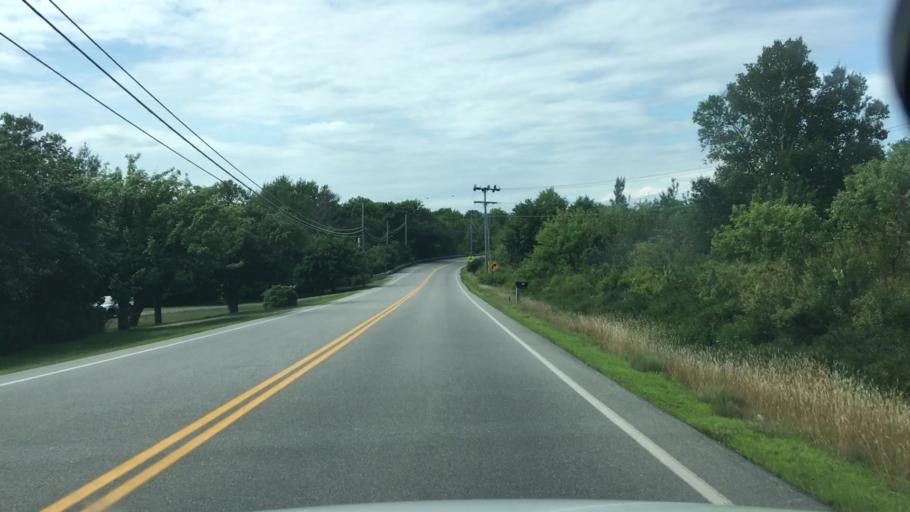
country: US
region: Maine
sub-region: Washington County
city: Eastport
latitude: 44.9132
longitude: -67.0041
